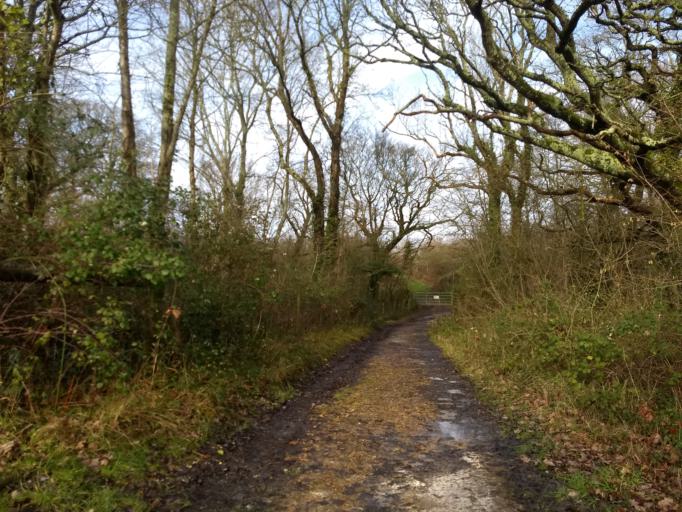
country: GB
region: England
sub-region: Isle of Wight
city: Newchurch
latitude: 50.7201
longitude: -1.2305
